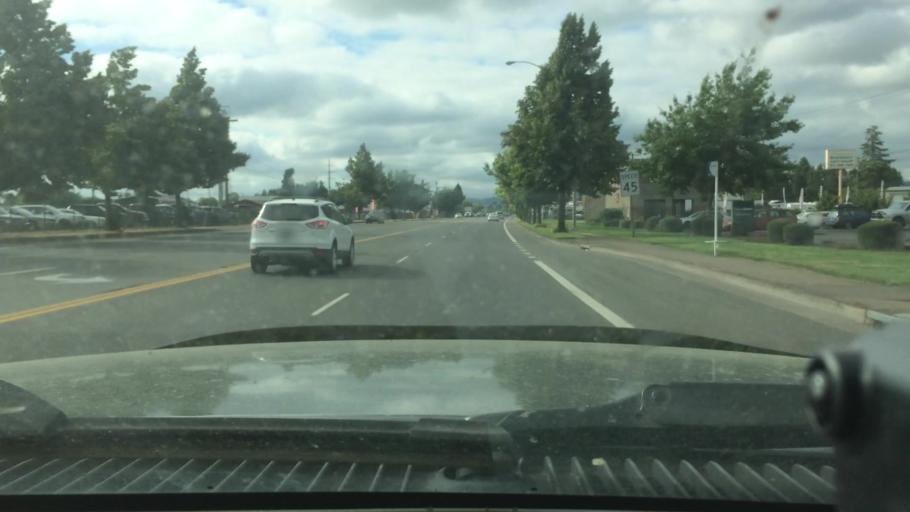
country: US
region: Oregon
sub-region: Lane County
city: Eugene
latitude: 44.0842
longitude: -123.1546
